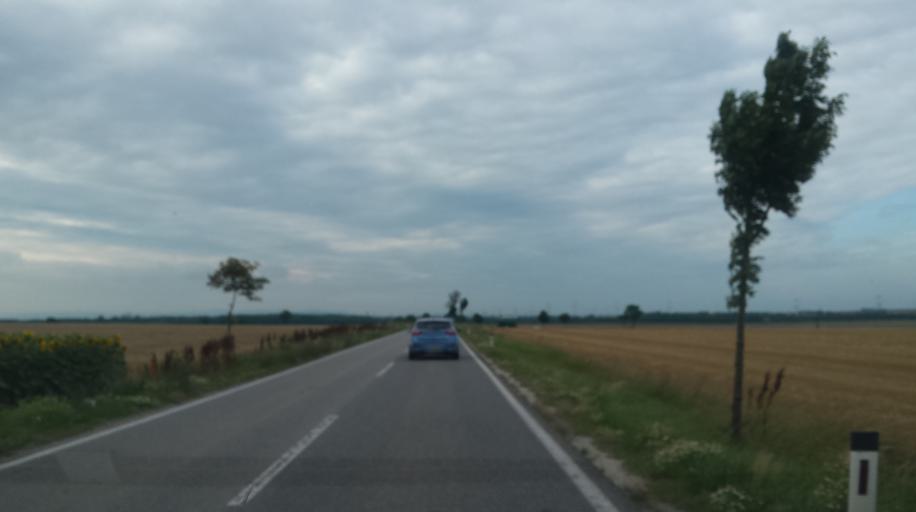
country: AT
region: Lower Austria
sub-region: Politischer Bezirk Wien-Umgebung
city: Moosbrunn
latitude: 48.0380
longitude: 16.4653
